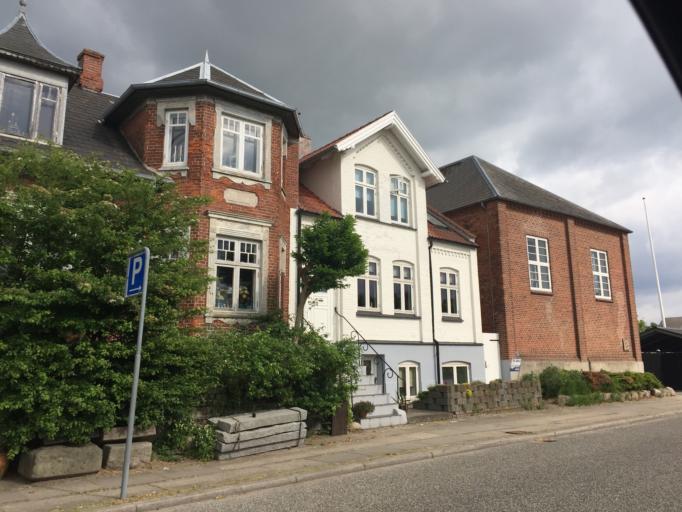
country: DK
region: South Denmark
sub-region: Assens Kommune
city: Assens
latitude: 55.2689
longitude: 9.8917
